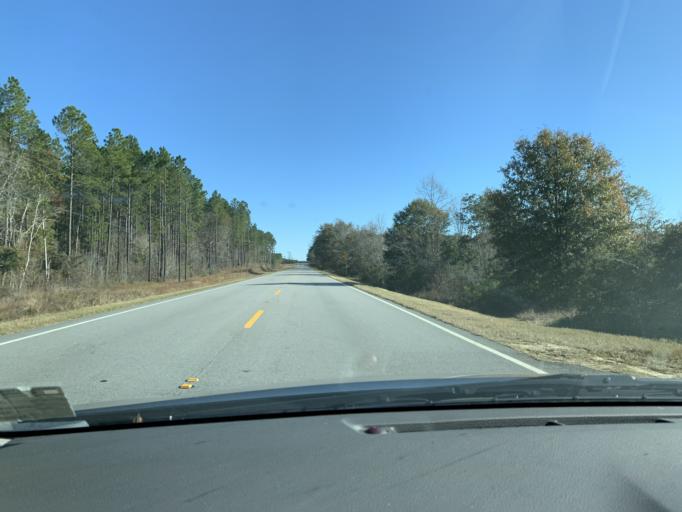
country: US
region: Georgia
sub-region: Ben Hill County
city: Fitzgerald
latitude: 31.7569
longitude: -83.1249
